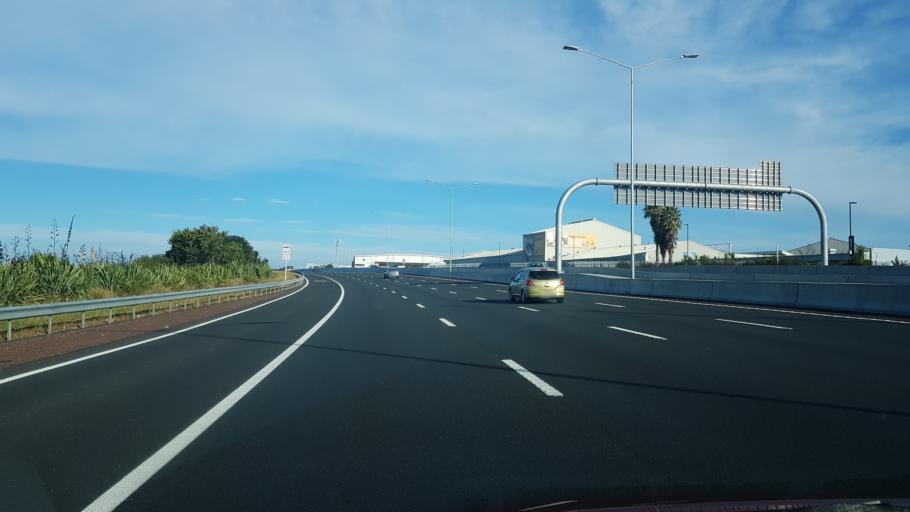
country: NZ
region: Auckland
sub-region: Auckland
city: Rosebank
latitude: -36.8656
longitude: 174.6666
